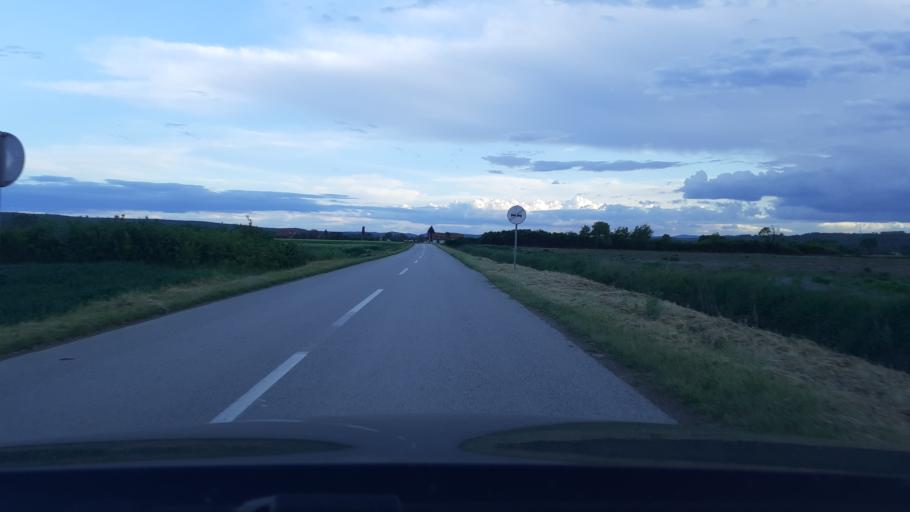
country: HR
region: Pozesko-Slavonska
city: Gradac
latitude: 45.3218
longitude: 17.8114
